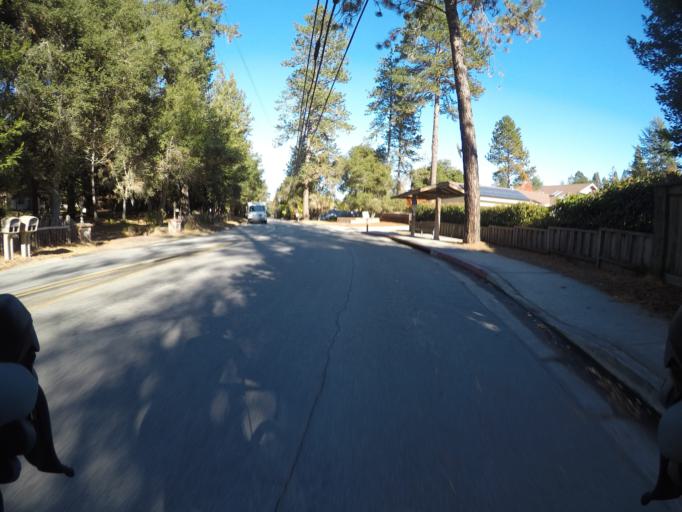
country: US
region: California
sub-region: Santa Cruz County
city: Mount Hermon
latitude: 37.0412
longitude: -122.0380
